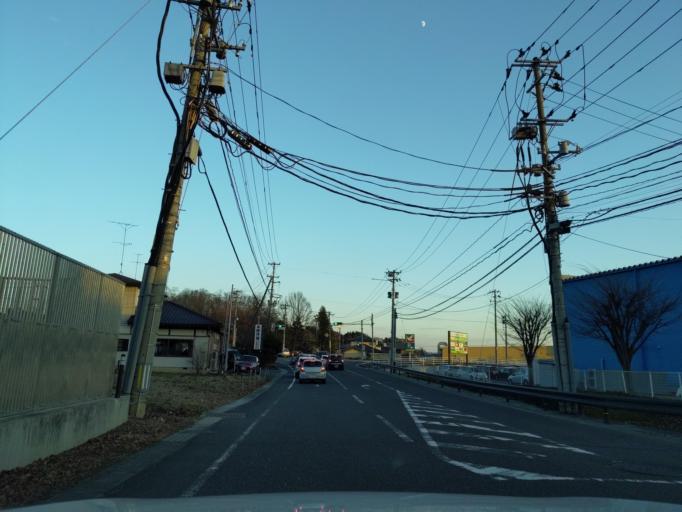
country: JP
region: Fukushima
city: Koriyama
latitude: 37.4478
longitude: 140.3840
